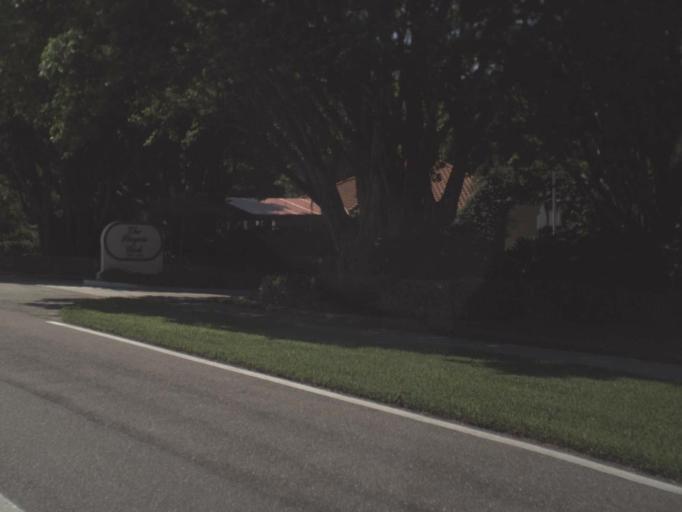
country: US
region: Florida
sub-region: Manatee County
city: Whitfield
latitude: 27.3517
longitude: -82.6093
